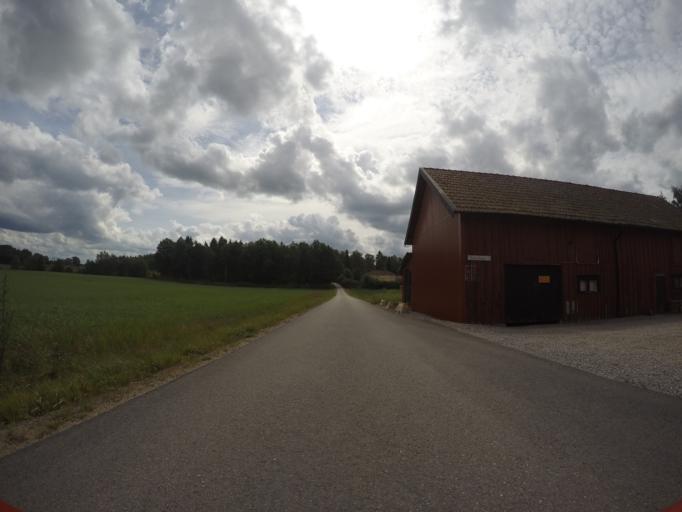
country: SE
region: Vaestra Goetaland
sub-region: Trollhattan
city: Trollhattan
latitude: 58.2334
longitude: 12.3137
